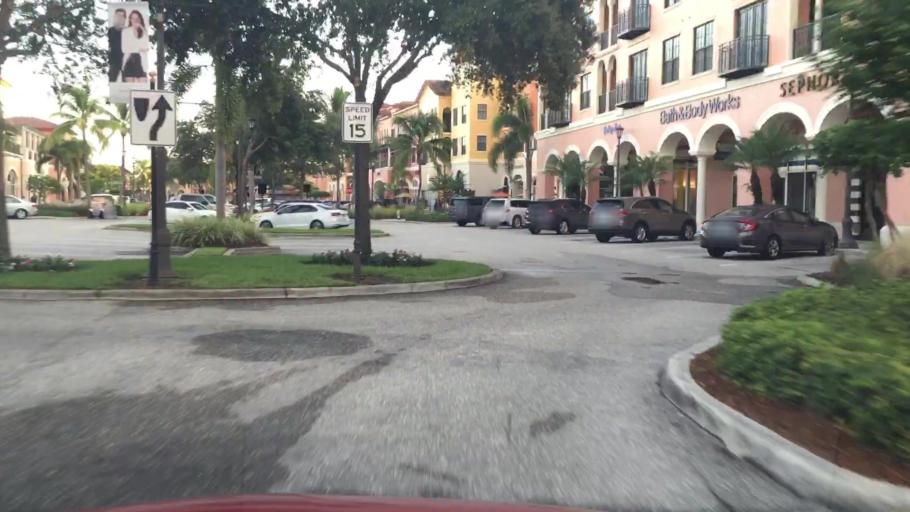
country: US
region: Florida
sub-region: Lee County
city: Estero
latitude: 26.4013
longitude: -81.8071
